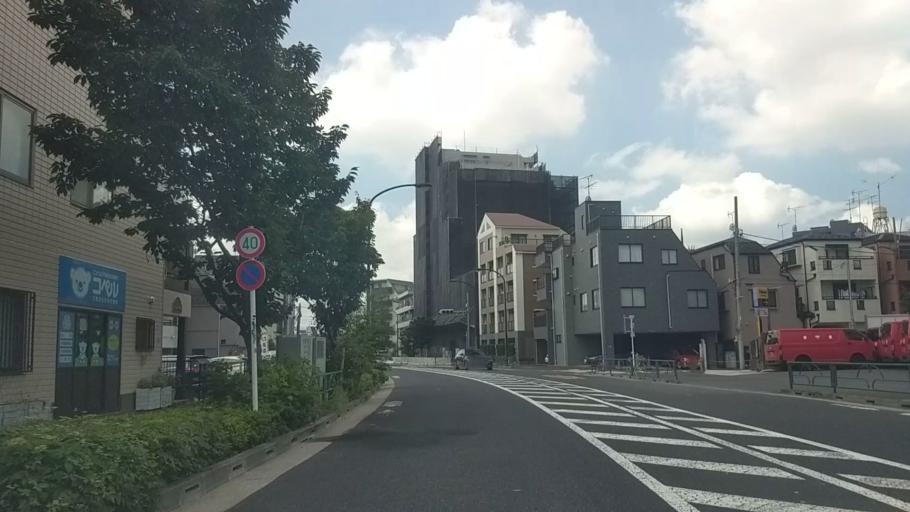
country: JP
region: Tokyo
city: Tokyo
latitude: 35.6219
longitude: 139.7029
